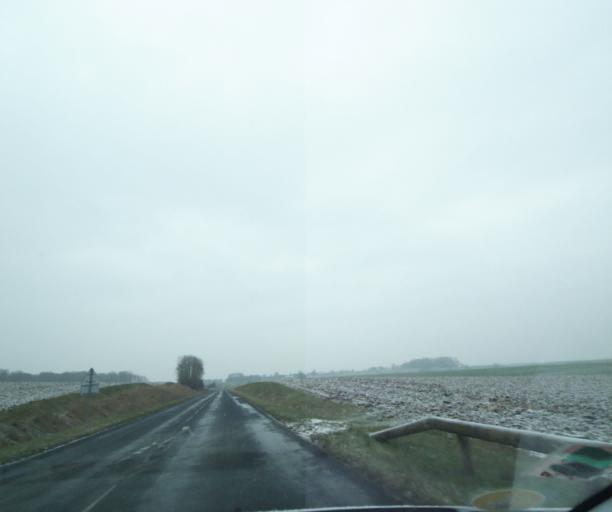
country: FR
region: Champagne-Ardenne
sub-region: Departement de la Haute-Marne
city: Wassy
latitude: 48.4695
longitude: 5.0245
